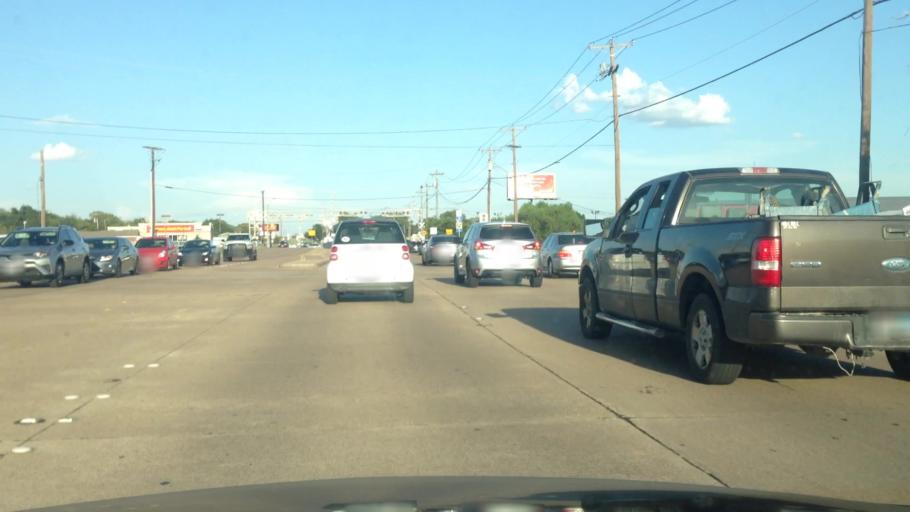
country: US
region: Texas
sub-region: Tarrant County
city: Watauga
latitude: 32.8608
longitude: -97.2666
